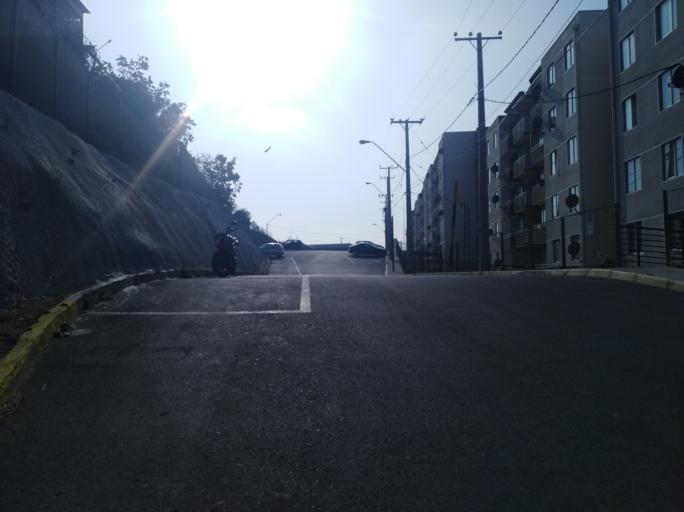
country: CL
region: Valparaiso
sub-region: Provincia de Marga Marga
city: Quilpue
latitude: -33.0662
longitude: -71.4350
